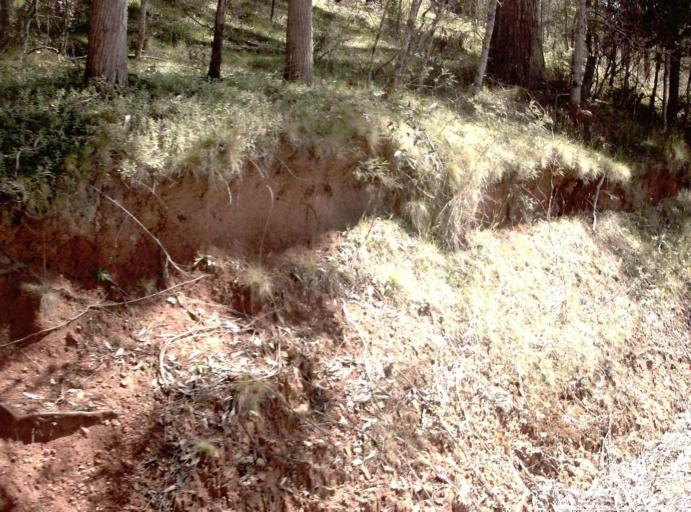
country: AU
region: New South Wales
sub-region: Bombala
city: Bombala
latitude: -37.0678
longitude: 148.7914
